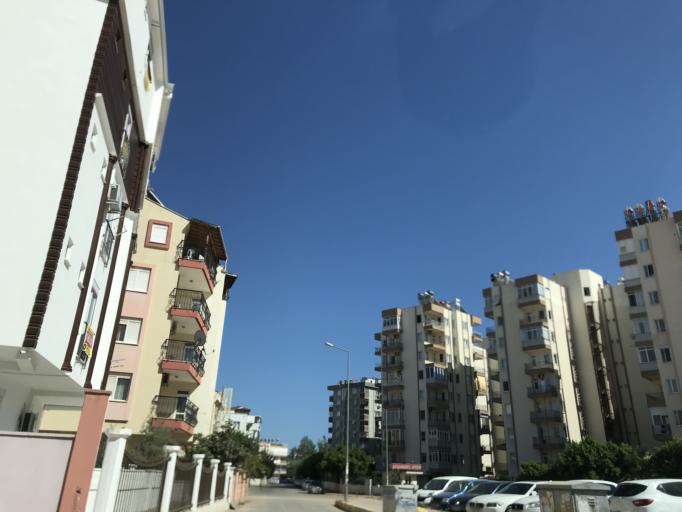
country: TR
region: Antalya
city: Antalya
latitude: 36.9022
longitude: 30.6570
